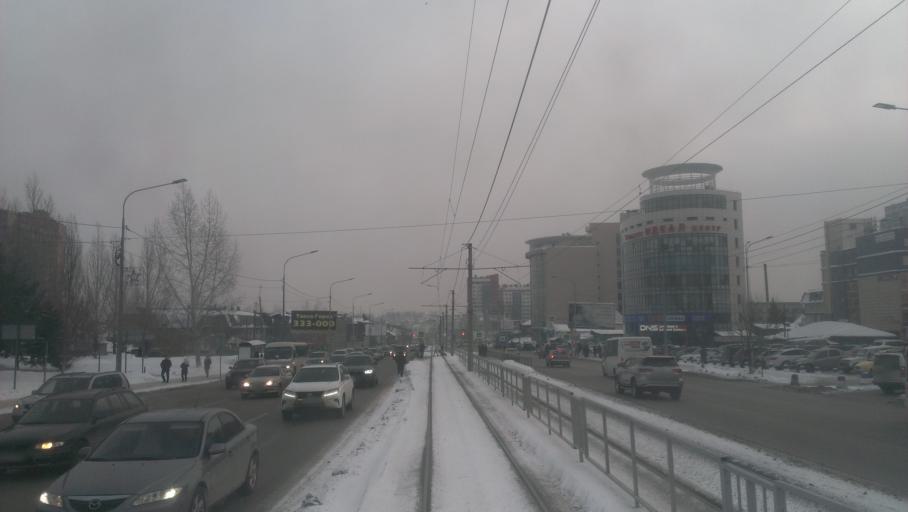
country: RU
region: Altai Krai
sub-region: Gorod Barnaulskiy
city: Barnaul
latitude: 53.3360
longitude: 83.7765
